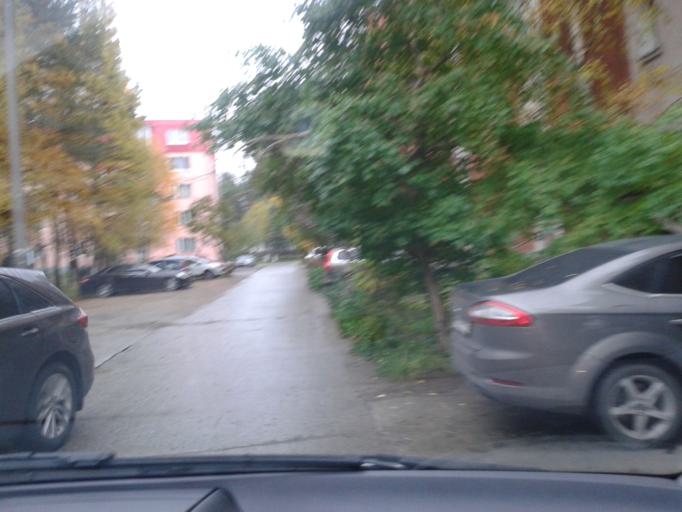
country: RU
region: Murmansk
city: Polyarnyye Zori
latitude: 67.3671
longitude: 32.4999
